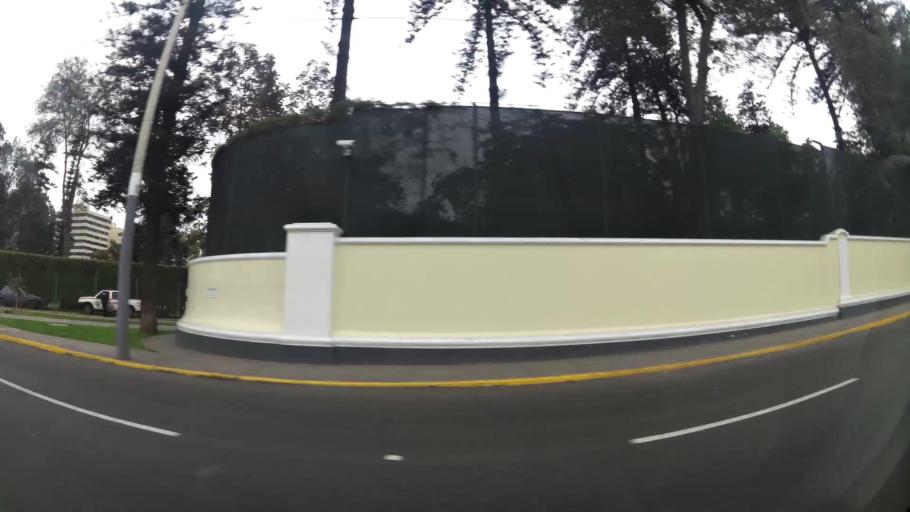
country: PE
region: Lima
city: Lima
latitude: -12.0709
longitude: -77.0353
